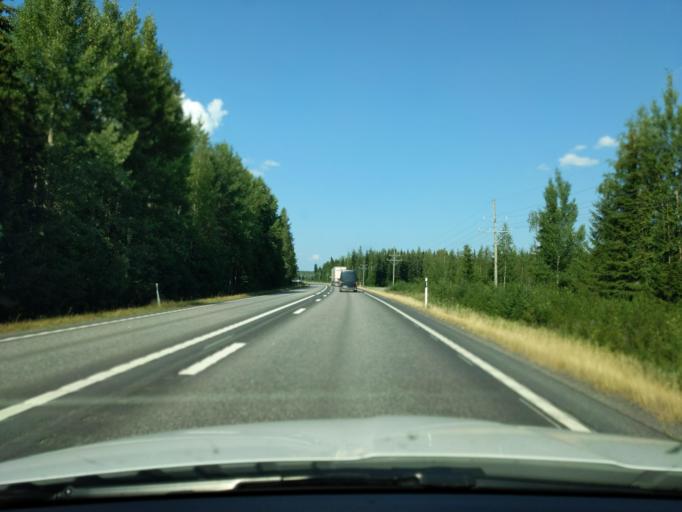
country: FI
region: Paijanne Tavastia
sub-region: Lahti
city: Jaervelae
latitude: 60.9153
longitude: 25.3530
